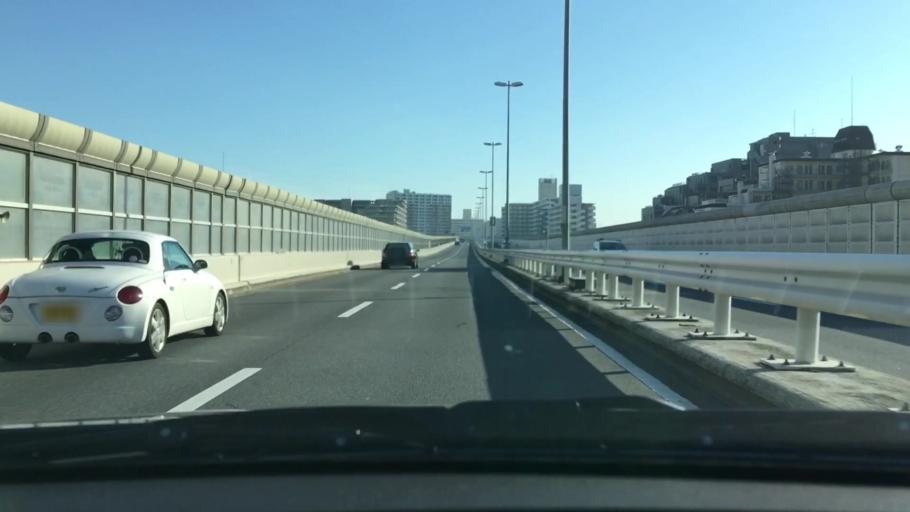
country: JP
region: Tokyo
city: Urayasu
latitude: 35.6943
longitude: 139.8393
